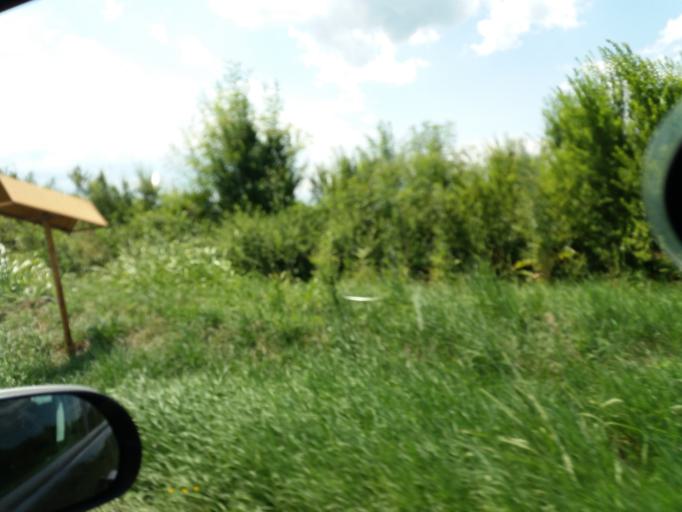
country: RS
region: Autonomna Pokrajina Vojvodina
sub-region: Sremski Okrug
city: Pecinci
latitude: 44.8648
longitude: 19.9596
